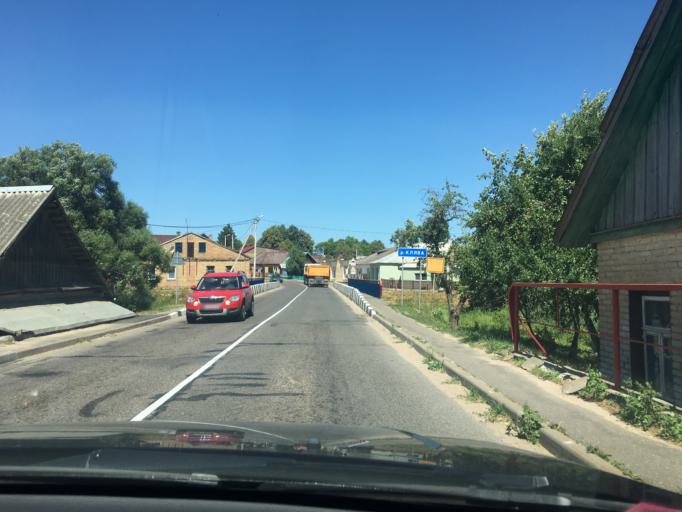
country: BY
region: Grodnenskaya
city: Hal'shany
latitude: 54.1562
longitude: 25.9074
